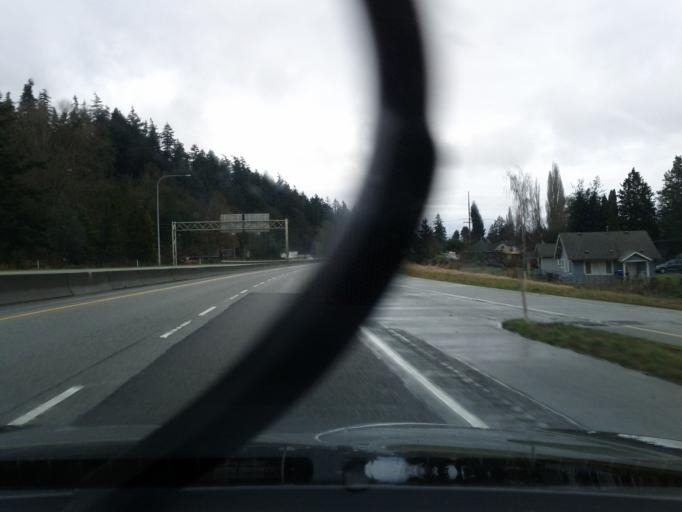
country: US
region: Washington
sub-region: Skagit County
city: Mount Vernon
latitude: 48.4156
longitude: -122.3321
